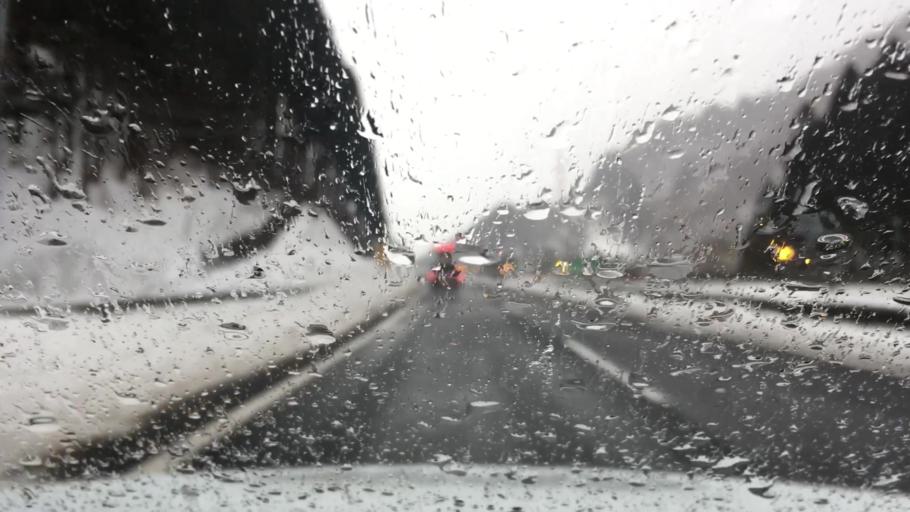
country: JP
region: Akita
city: Hanawa
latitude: 40.1363
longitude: 140.8144
